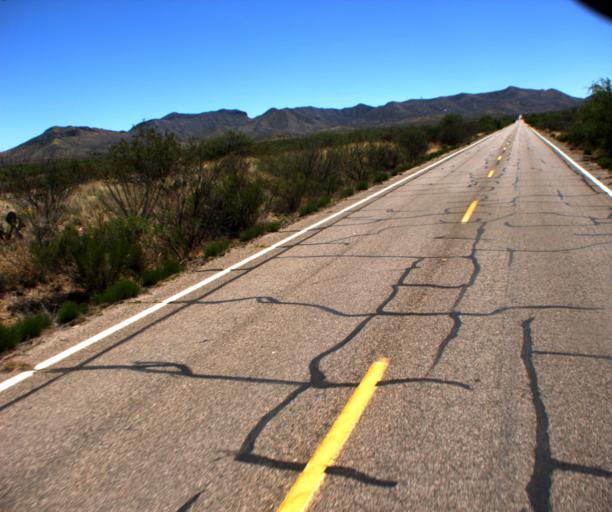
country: US
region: Arizona
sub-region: Pima County
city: Vail
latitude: 31.9571
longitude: -110.6695
